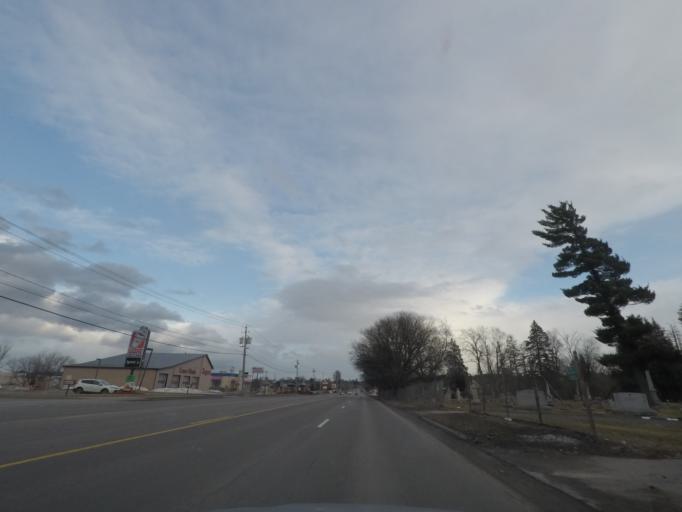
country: US
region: New York
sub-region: Oneida County
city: New Hartford
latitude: 43.0816
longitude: -75.3226
